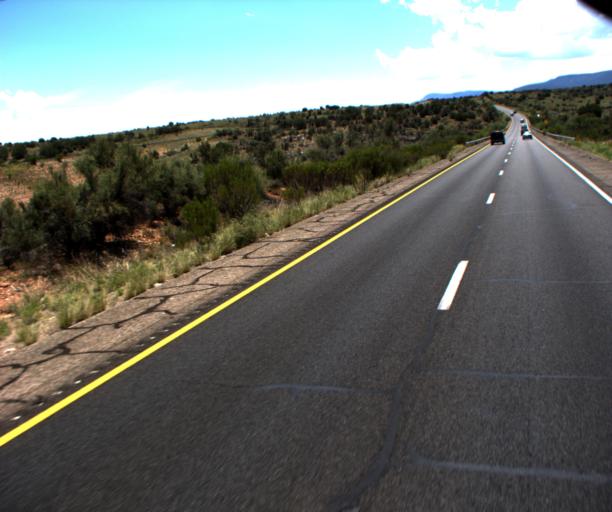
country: US
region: Arizona
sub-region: Yavapai County
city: Verde Village
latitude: 34.6713
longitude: -111.9707
